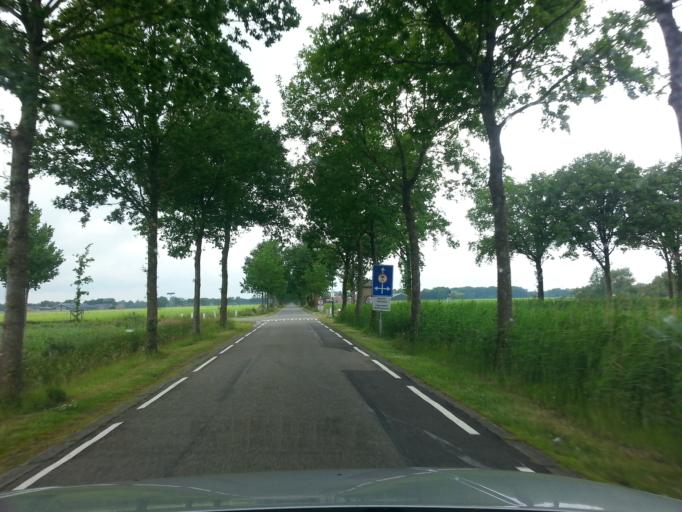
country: NL
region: Utrecht
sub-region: Gemeente Leusden
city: Leusden
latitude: 52.1057
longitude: 5.4557
